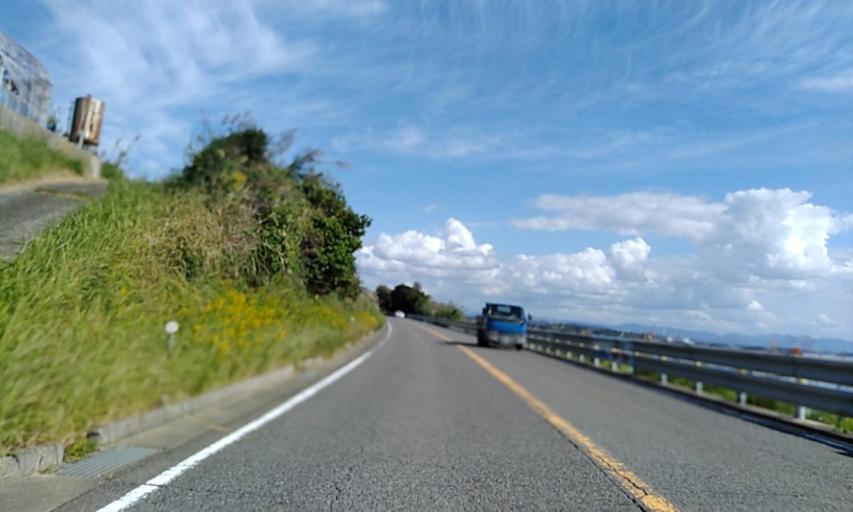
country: JP
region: Wakayama
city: Tanabe
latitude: 33.7830
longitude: 135.2613
